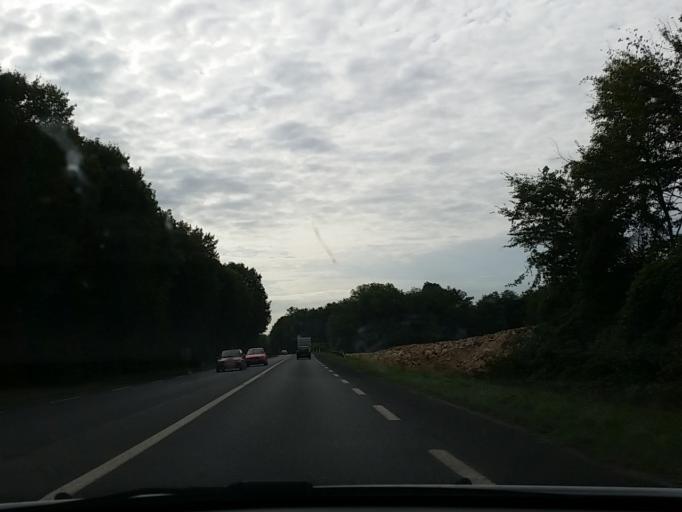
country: FR
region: Centre
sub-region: Departement du Loir-et-Cher
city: Cellettes
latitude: 47.5371
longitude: 1.4110
